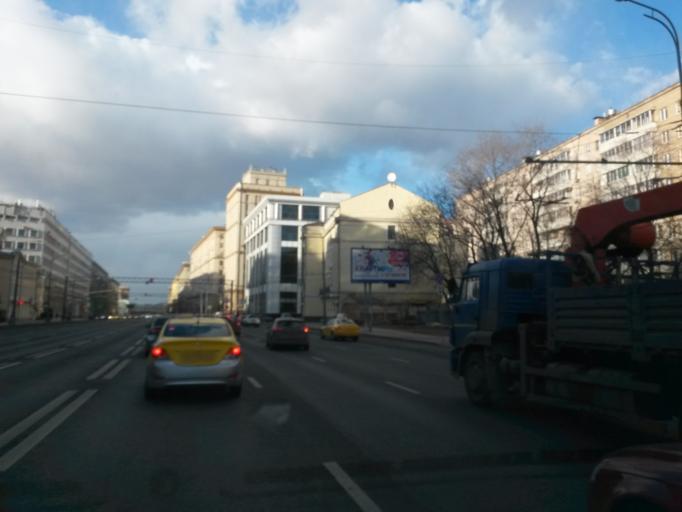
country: RU
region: Moscow
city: Mar'ina Roshcha
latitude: 55.7848
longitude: 37.6350
